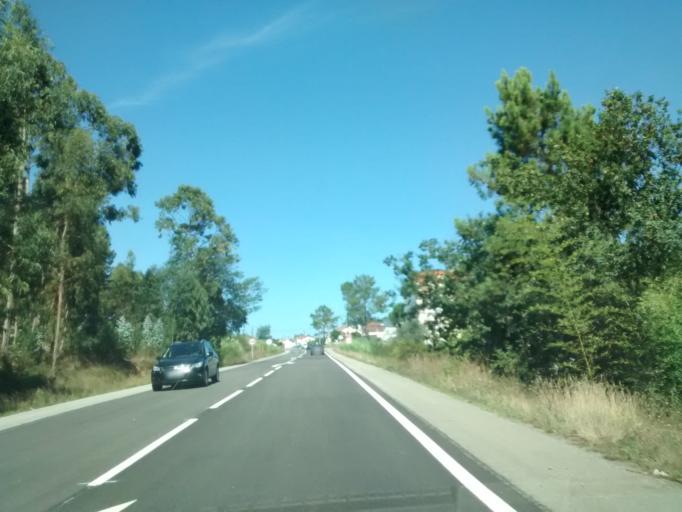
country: PT
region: Aveiro
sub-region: Oliveira do Bairro
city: Oia
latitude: 40.5354
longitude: -8.5133
